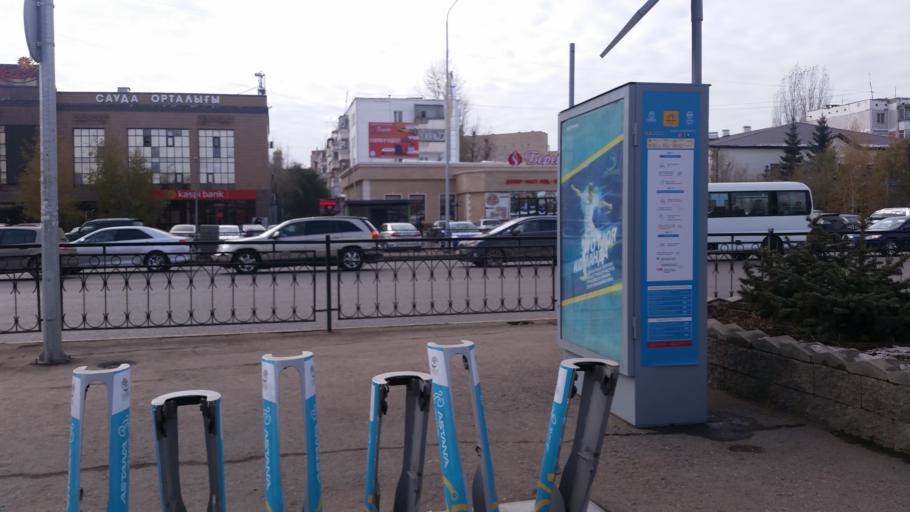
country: KZ
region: Astana Qalasy
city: Astana
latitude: 51.1548
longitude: 71.4861
